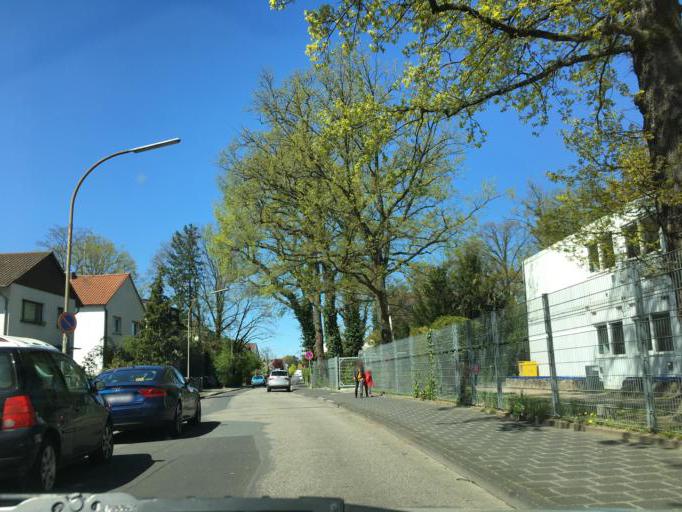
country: DE
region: Hesse
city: Obertshausen
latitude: 50.0729
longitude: 8.8566
